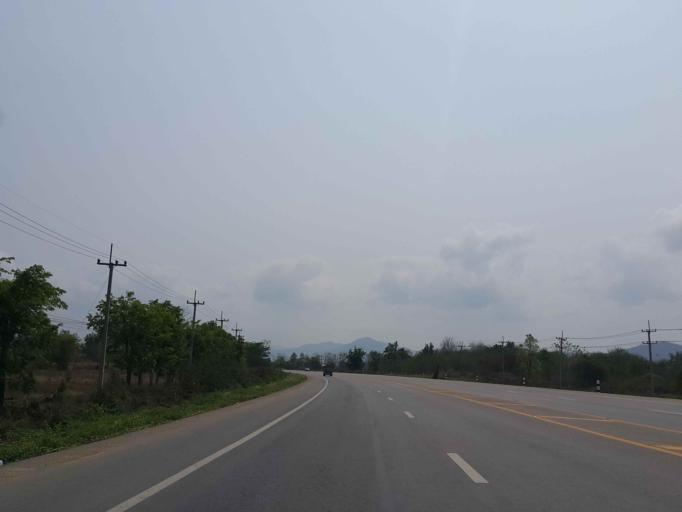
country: TH
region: Chiang Mai
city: San Kamphaeng
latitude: 18.7110
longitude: 99.1318
